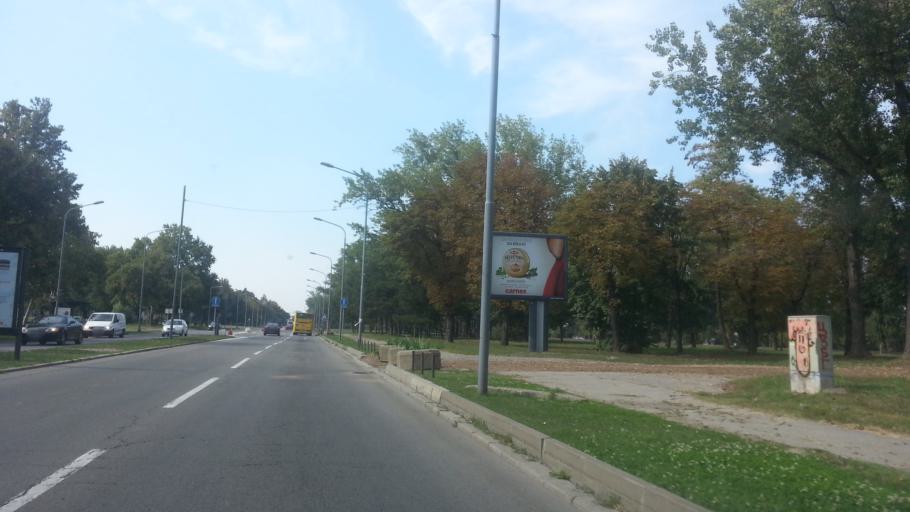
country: RS
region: Central Serbia
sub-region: Belgrade
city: Novi Beograd
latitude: 44.8201
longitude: 20.4321
